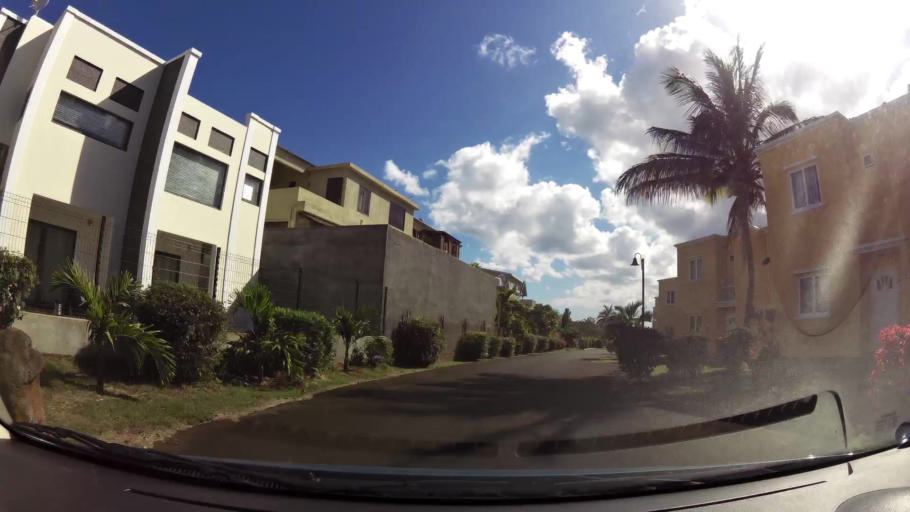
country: MU
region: Black River
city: Albion
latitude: -20.2219
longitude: 57.4147
